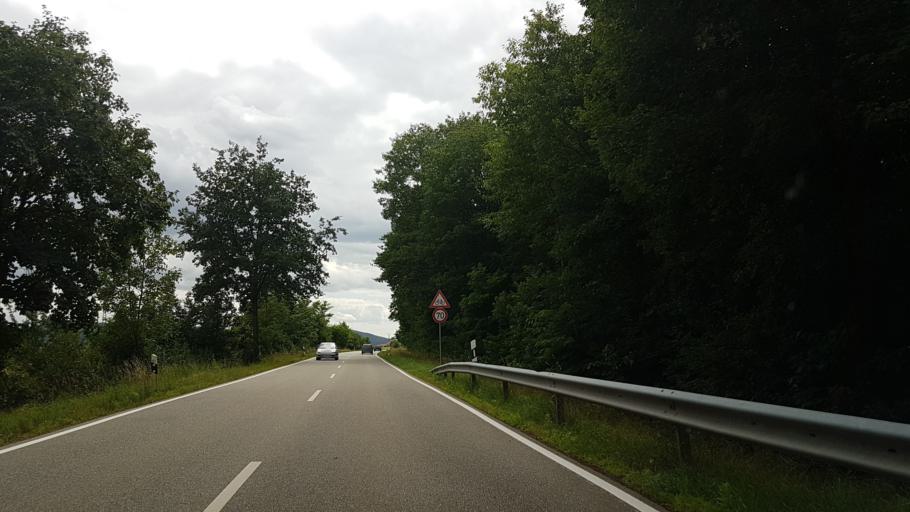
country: DE
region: Rheinland-Pfalz
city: Hutschenhausen
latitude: 49.4109
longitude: 7.4543
